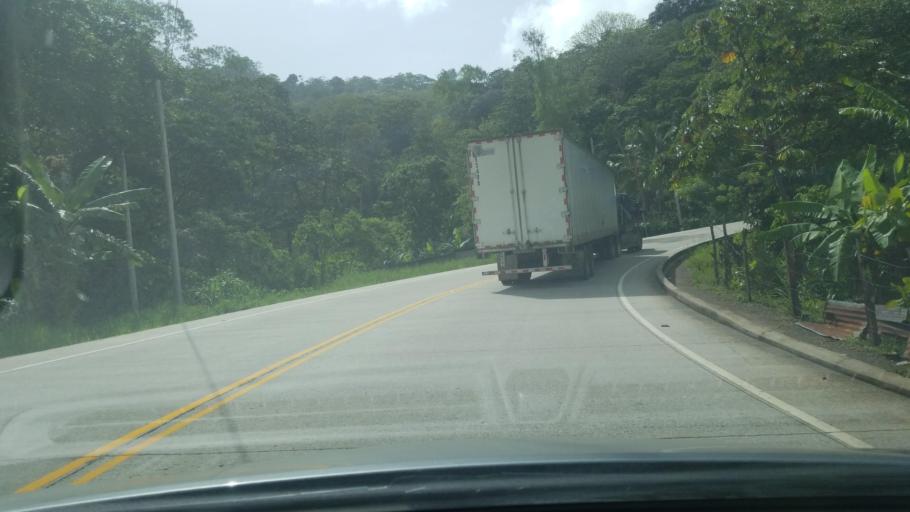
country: HN
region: Copan
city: San Jeronimo
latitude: 14.9339
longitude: -88.9541
